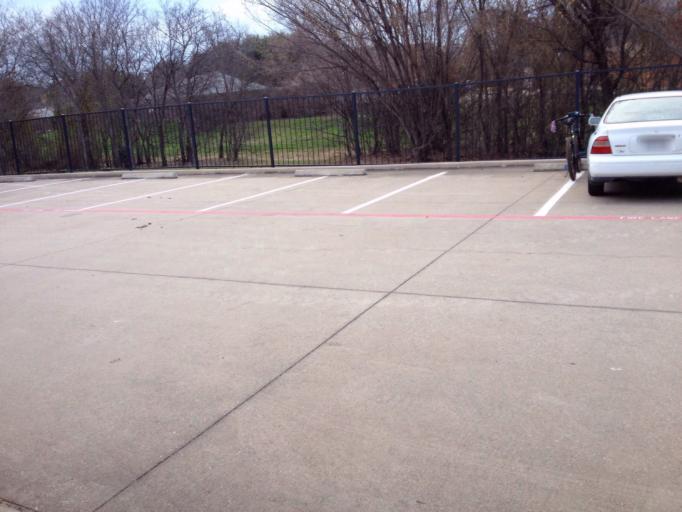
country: US
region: Texas
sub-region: Denton County
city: Highland Village
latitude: 33.0537
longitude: -97.0341
